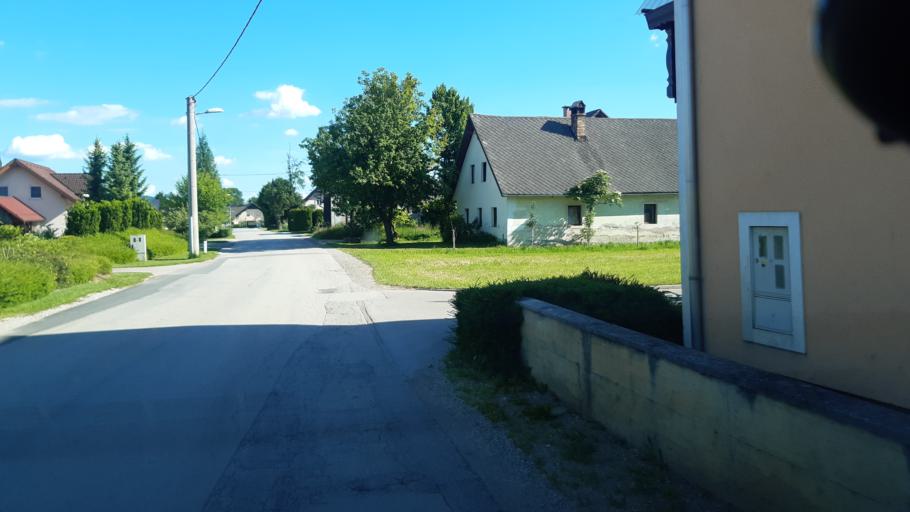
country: SI
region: Sencur
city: Hrastje
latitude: 46.1978
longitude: 14.3993
